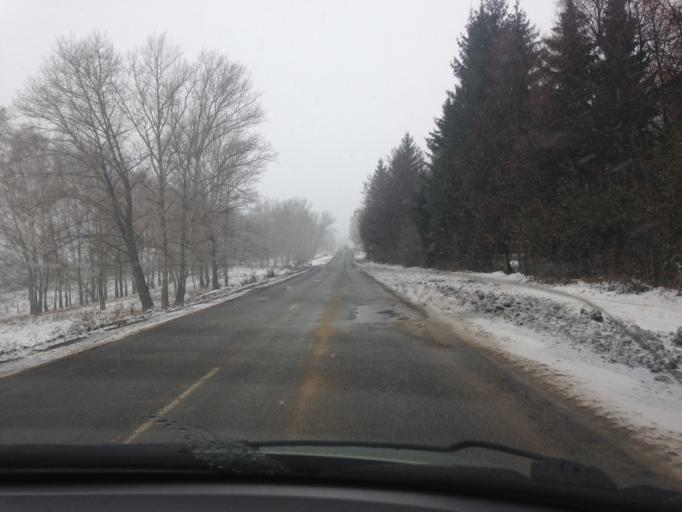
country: RU
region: Tula
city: Shchekino
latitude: 53.8504
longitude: 37.4799
